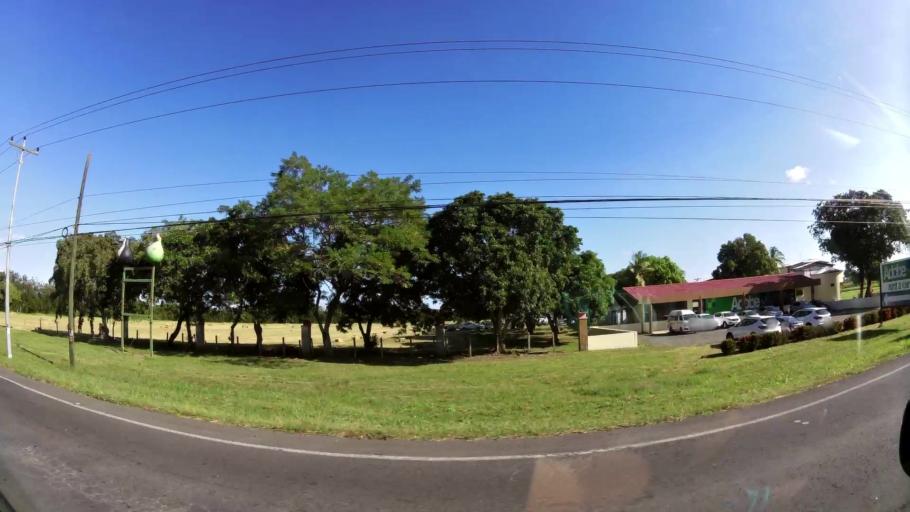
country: CR
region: Guanacaste
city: Sardinal
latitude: 10.5730
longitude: -85.5836
